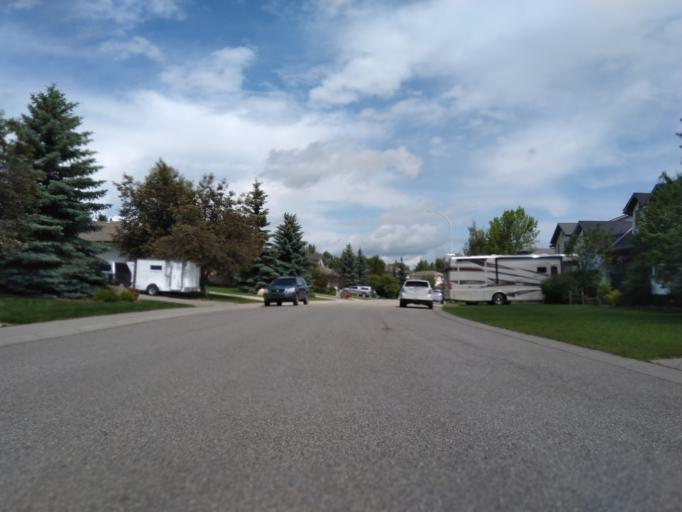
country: CA
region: Alberta
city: Cochrane
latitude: 51.1864
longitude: -114.4994
